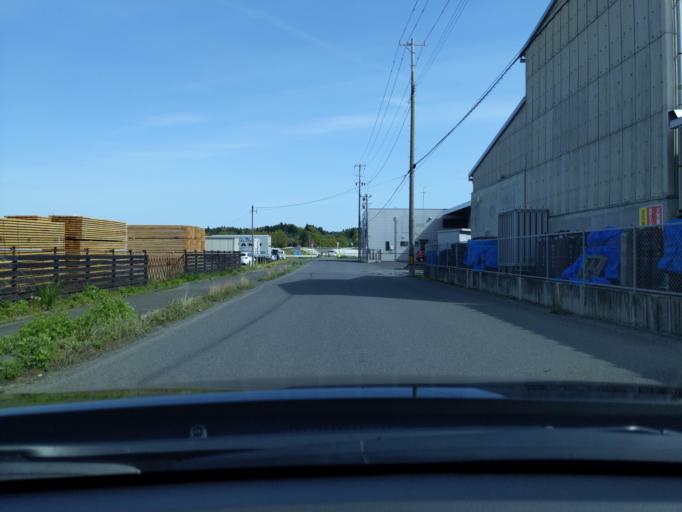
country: JP
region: Fukushima
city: Koriyama
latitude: 37.3691
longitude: 140.3990
